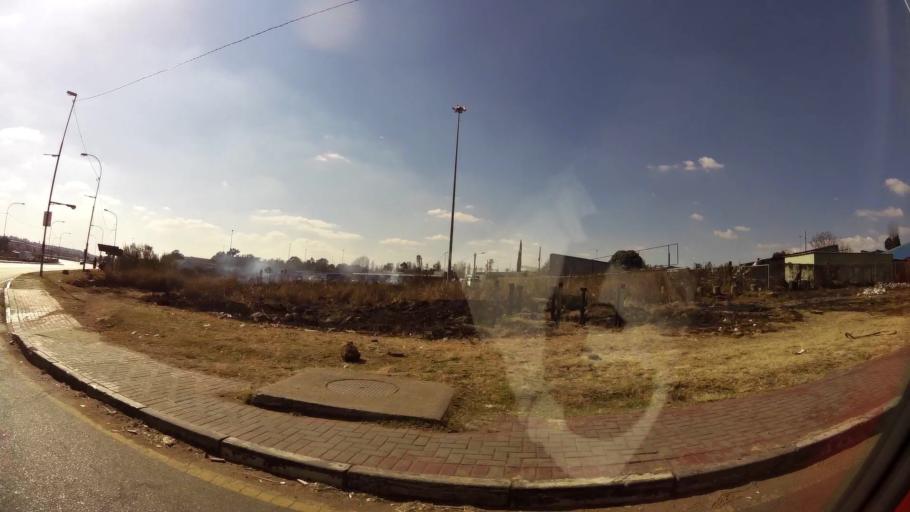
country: ZA
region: Gauteng
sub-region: City of Johannesburg Metropolitan Municipality
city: Soweto
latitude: -26.2410
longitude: 27.9126
